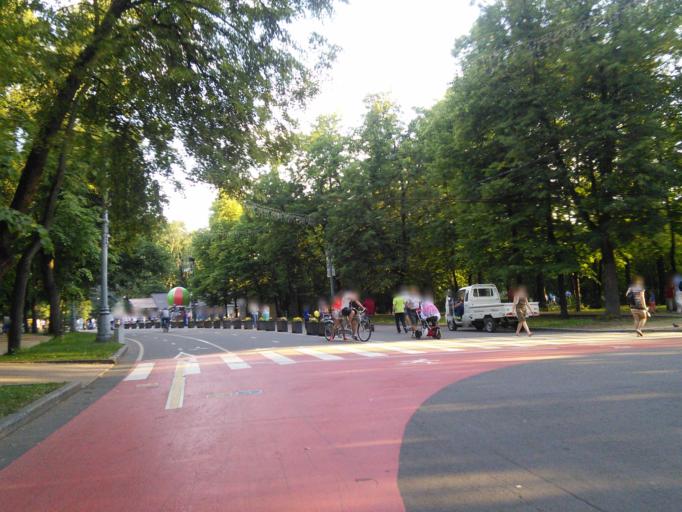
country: RU
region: Moscow
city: Sokol'niki
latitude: 55.7952
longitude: 37.6749
